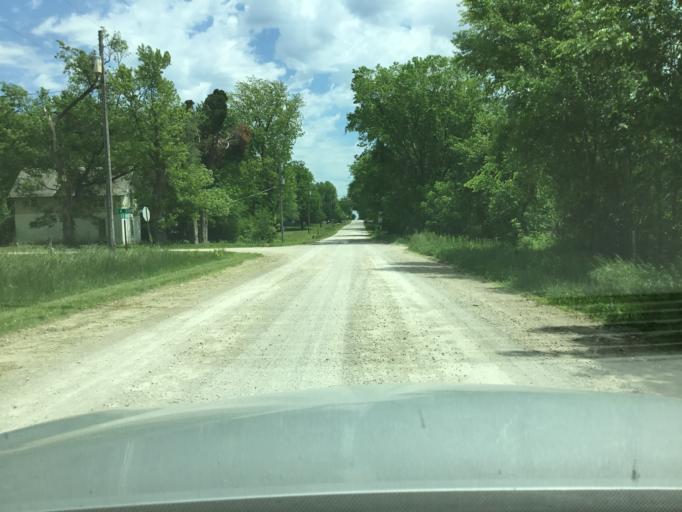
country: US
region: Kansas
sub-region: Montgomery County
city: Independence
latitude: 37.1095
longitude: -95.7654
